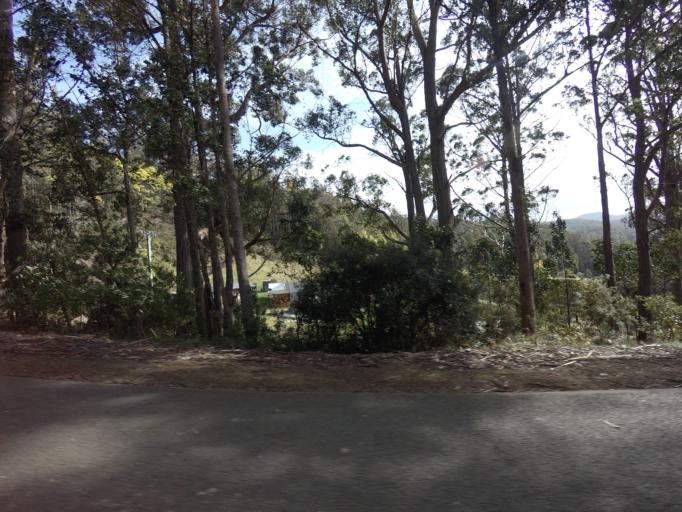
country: AU
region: Tasmania
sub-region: Kingborough
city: Margate
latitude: -43.0093
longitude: 147.1670
